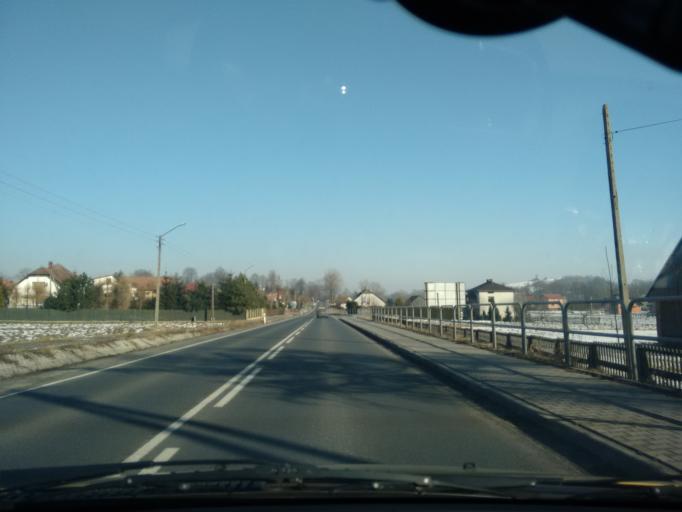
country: PL
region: Lesser Poland Voivodeship
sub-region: Powiat wadowicki
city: Inwald
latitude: 49.8635
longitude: 19.3945
